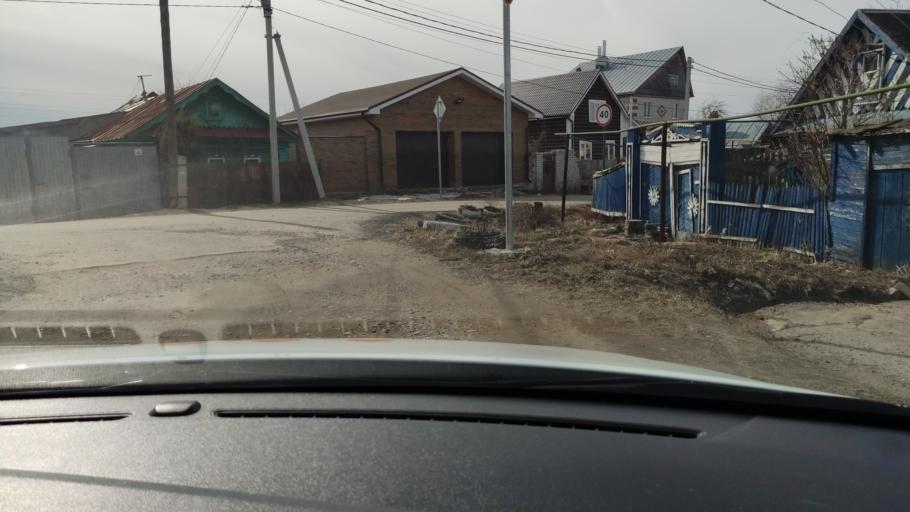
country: RU
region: Tatarstan
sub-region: Gorod Kazan'
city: Kazan
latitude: 55.7257
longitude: 49.1408
